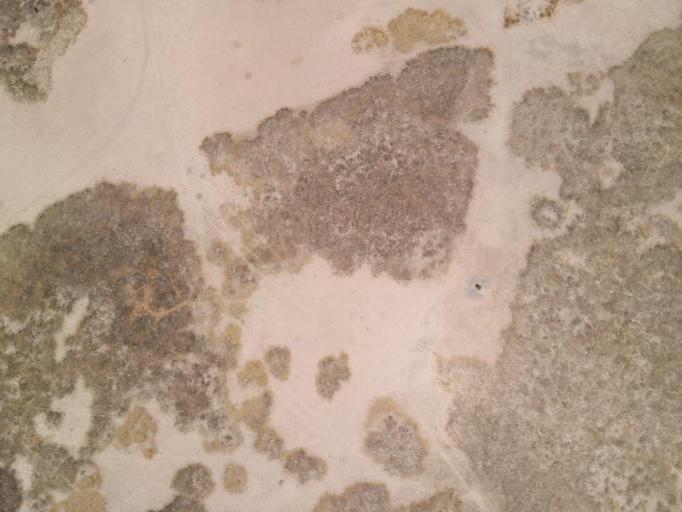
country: BO
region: La Paz
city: Batallas
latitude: -16.3521
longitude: -68.6300
